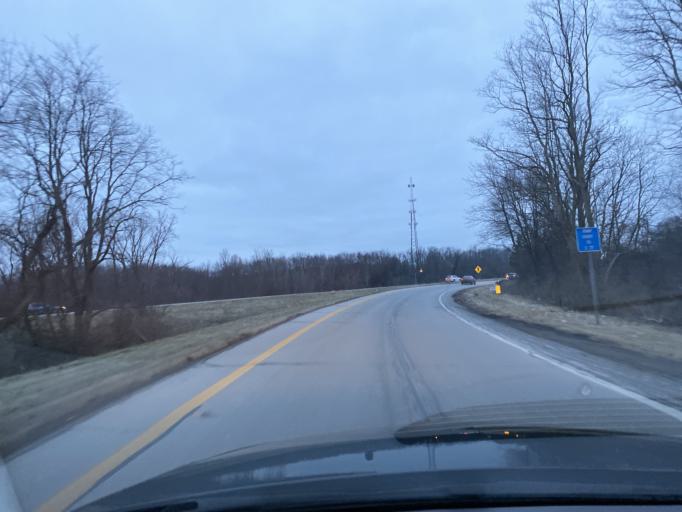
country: US
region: Ohio
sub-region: Summit County
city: Montrose-Ghent
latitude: 41.1500
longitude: -81.6345
